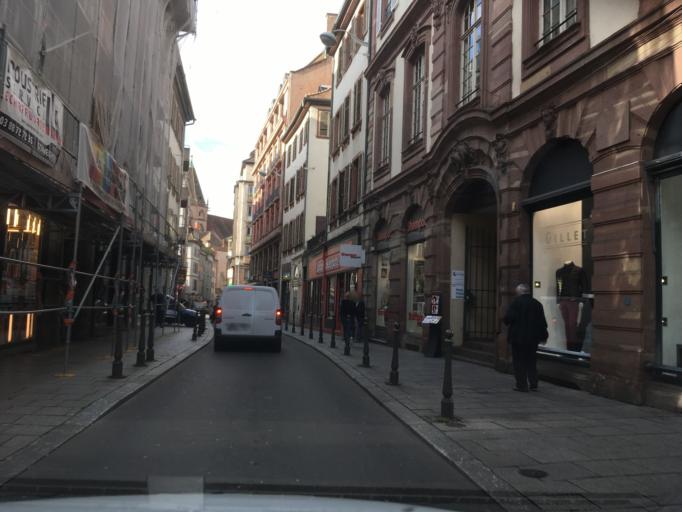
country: FR
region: Alsace
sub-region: Departement du Bas-Rhin
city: Strasbourg
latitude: 48.5810
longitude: 7.7477
